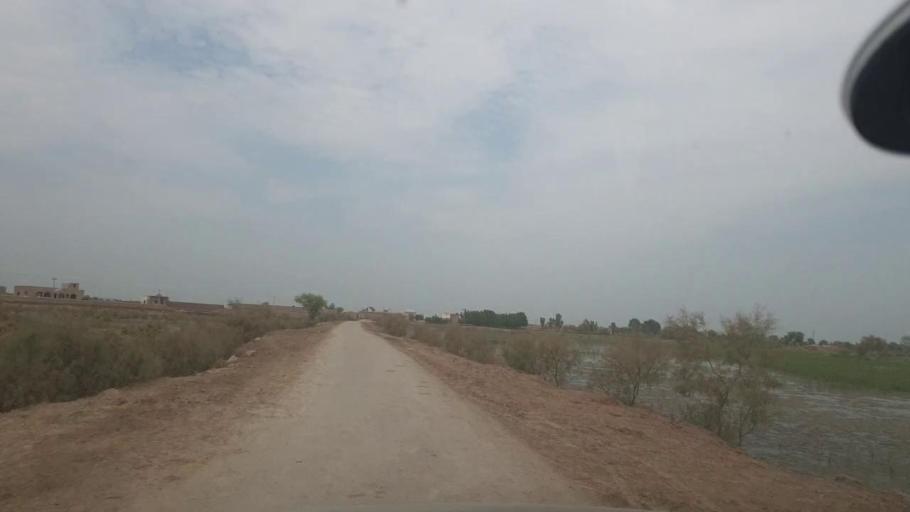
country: PK
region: Balochistan
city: Mehrabpur
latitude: 28.0570
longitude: 68.1487
